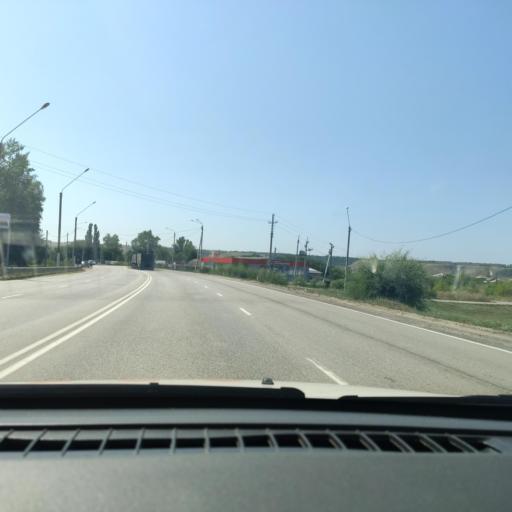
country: RU
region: Voronezj
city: Uryv-Pokrovka
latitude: 51.0462
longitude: 38.9819
